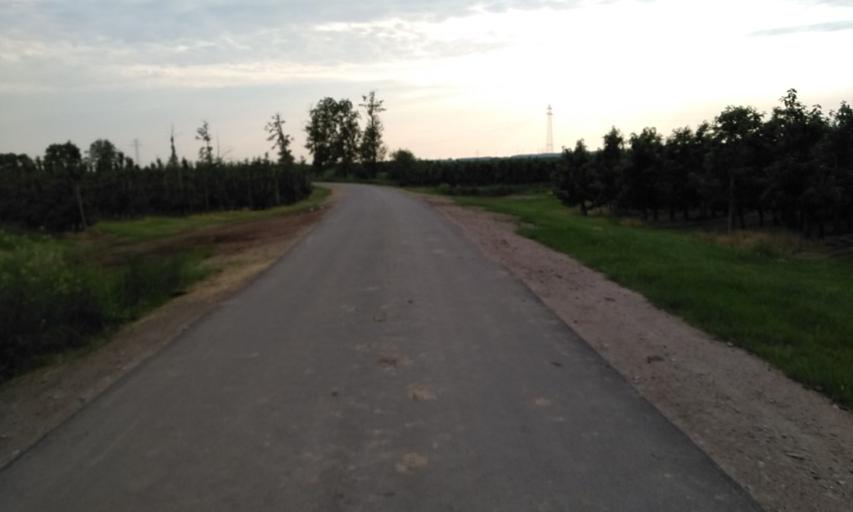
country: DE
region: Lower Saxony
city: Mittelnkirchen
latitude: 53.5229
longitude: 9.6397
